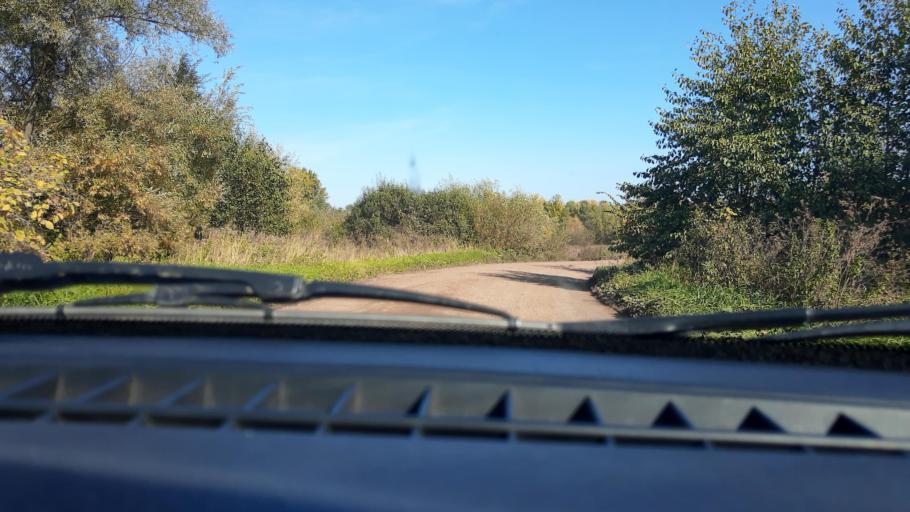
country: RU
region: Bashkortostan
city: Mikhaylovka
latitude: 54.7354
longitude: 55.8317
